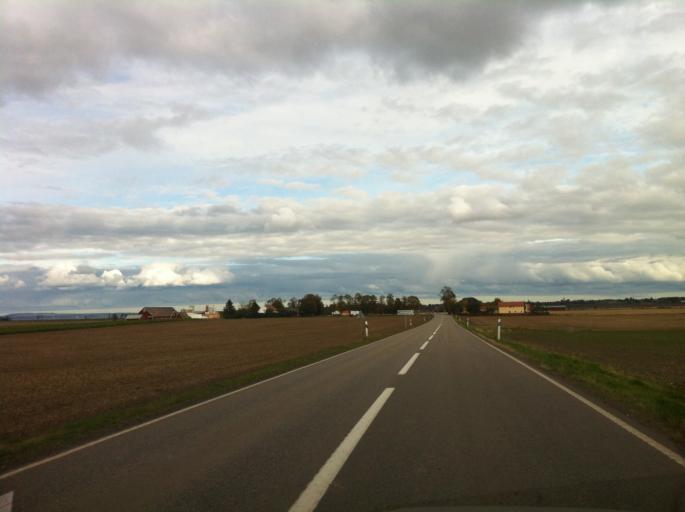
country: SE
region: OEstergoetland
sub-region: Vadstena Kommun
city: Vadstena
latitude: 58.4265
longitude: 14.8386
